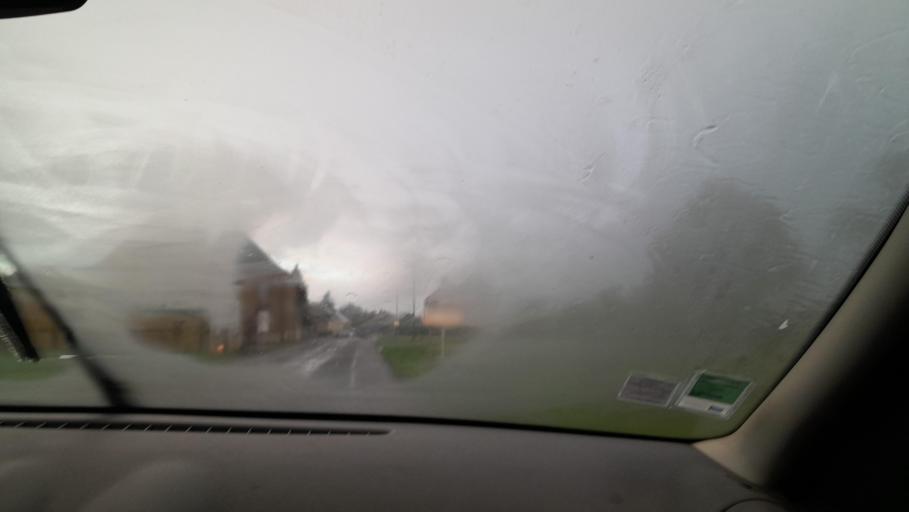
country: FR
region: Pays de la Loire
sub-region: Departement de la Mayenne
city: Ballots
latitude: 47.8904
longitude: -1.0470
